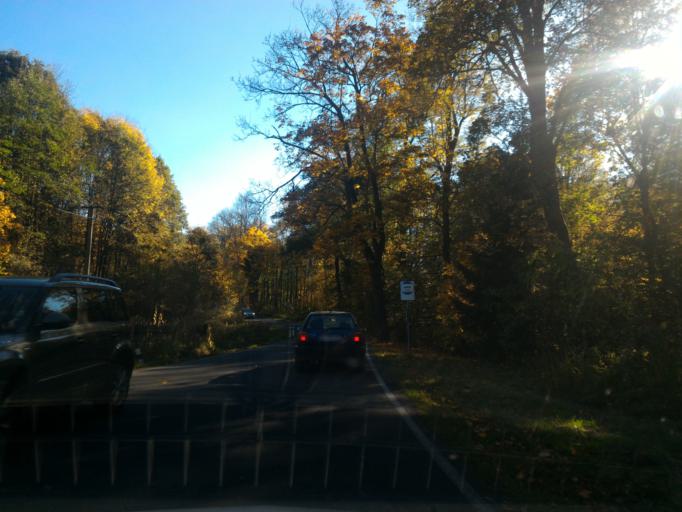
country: CZ
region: Ustecky
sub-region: Okres Decin
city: Sluknov
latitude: 51.0171
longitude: 14.4562
